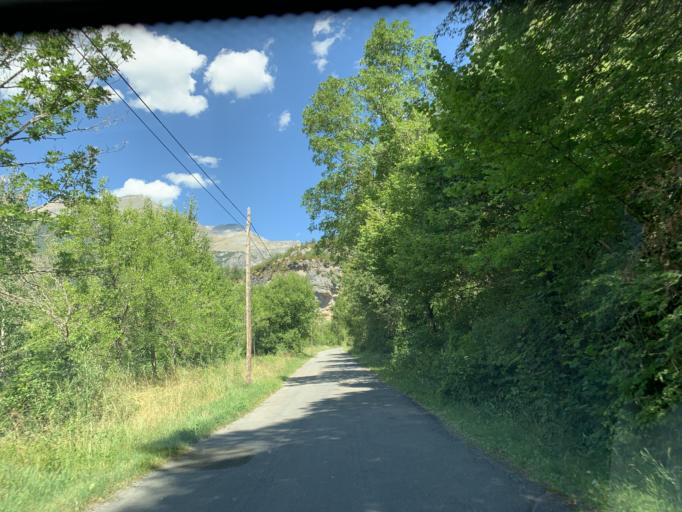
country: ES
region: Aragon
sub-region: Provincia de Huesca
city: Hoz de Jaca
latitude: 42.7144
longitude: -0.3008
